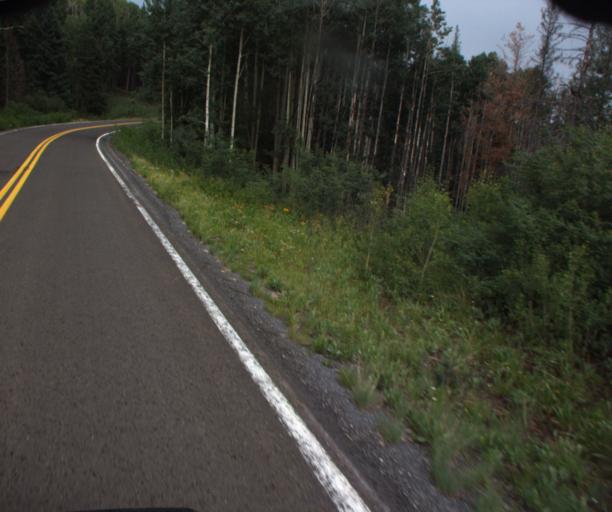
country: US
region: Arizona
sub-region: Greenlee County
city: Morenci
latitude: 33.5731
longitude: -109.3583
